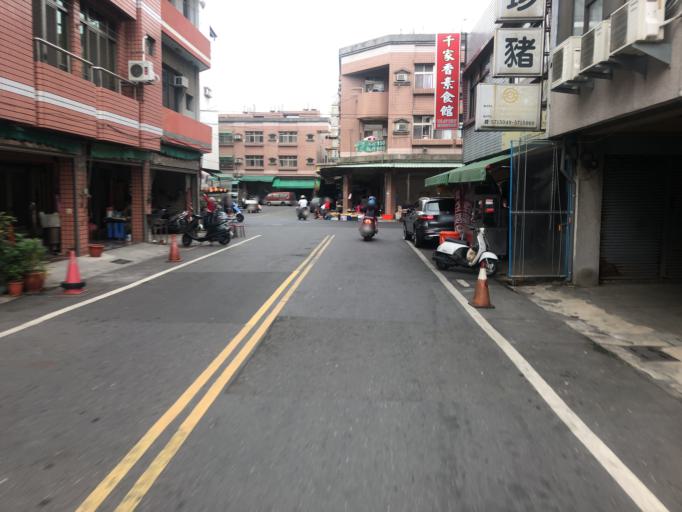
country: TW
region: Taiwan
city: Xinying
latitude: 23.1848
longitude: 120.2497
